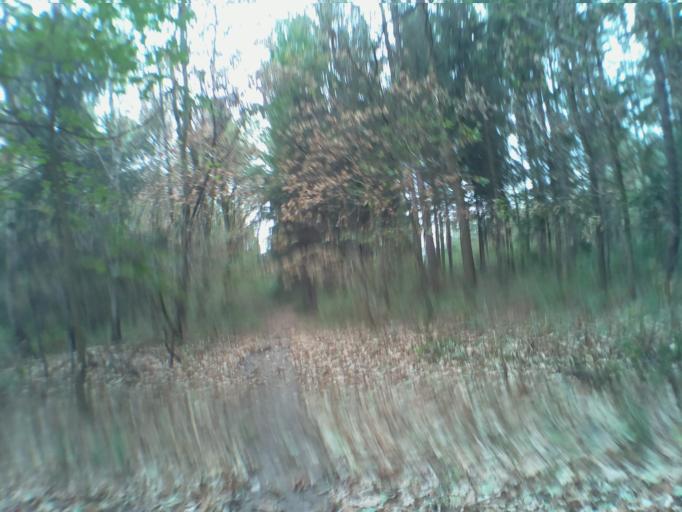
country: PL
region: Lower Silesian Voivodeship
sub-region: Powiat swidnicki
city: Strzegom
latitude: 50.9921
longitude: 16.2941
